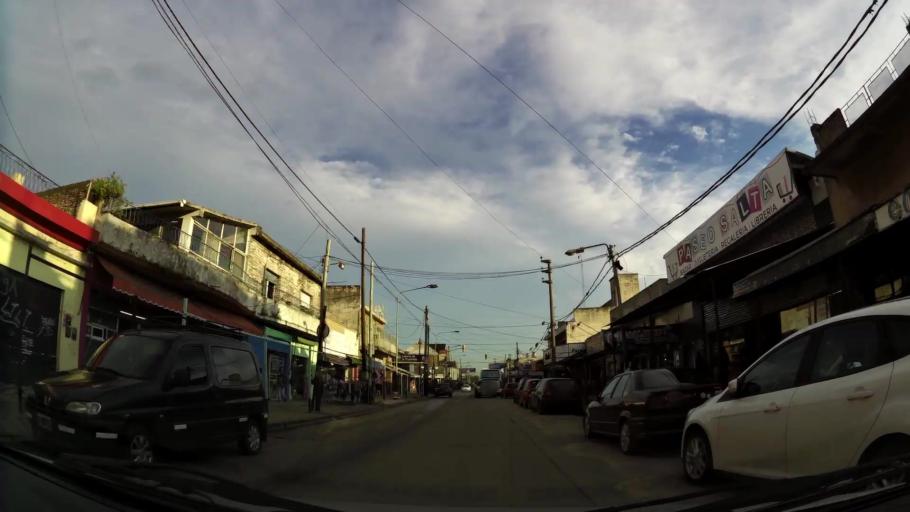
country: AR
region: Buenos Aires
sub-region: Partido de Almirante Brown
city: Adrogue
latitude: -34.7676
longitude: -58.3569
